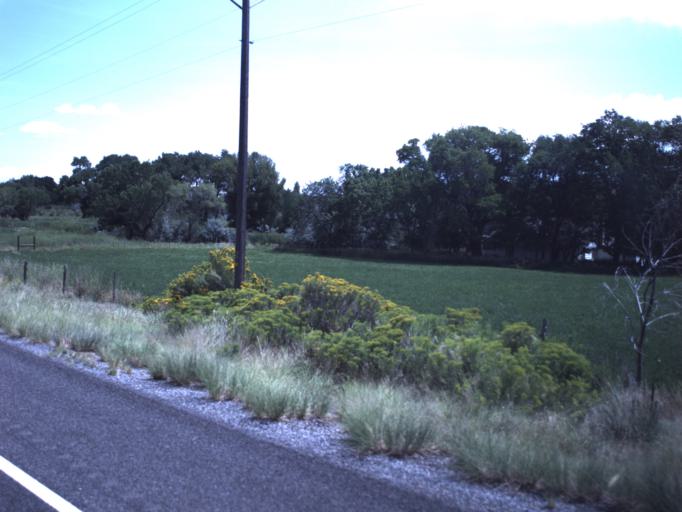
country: US
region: Utah
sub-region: Emery County
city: Huntington
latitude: 39.3526
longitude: -111.0098
